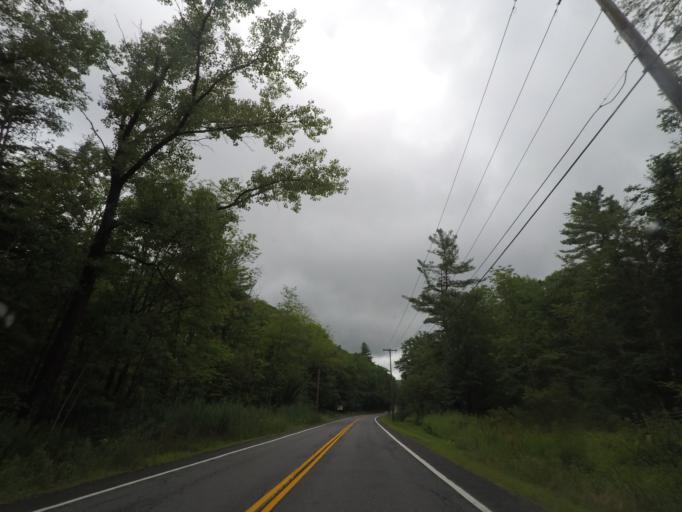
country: US
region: New York
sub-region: Rensselaer County
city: Averill Park
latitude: 42.5906
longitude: -73.4969
